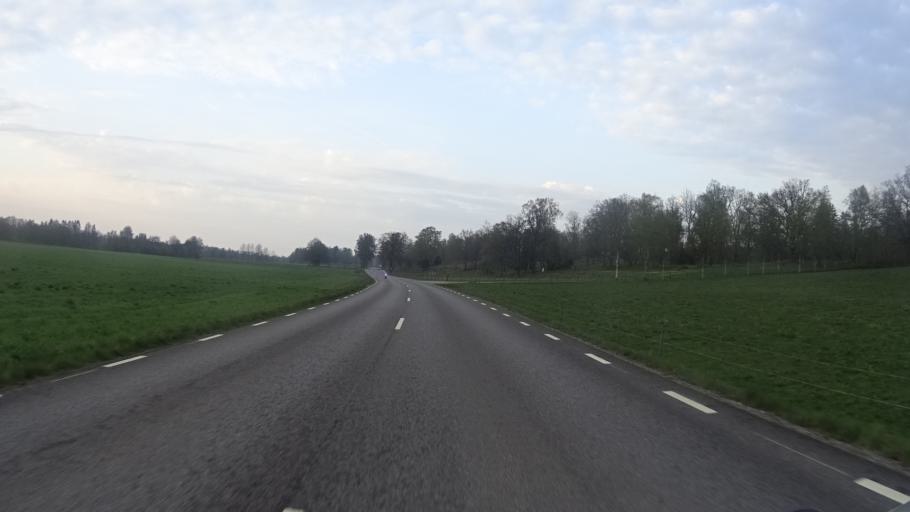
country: SE
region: Kronoberg
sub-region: Ljungby Kommun
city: Ljungby
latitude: 56.8450
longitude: 13.9728
